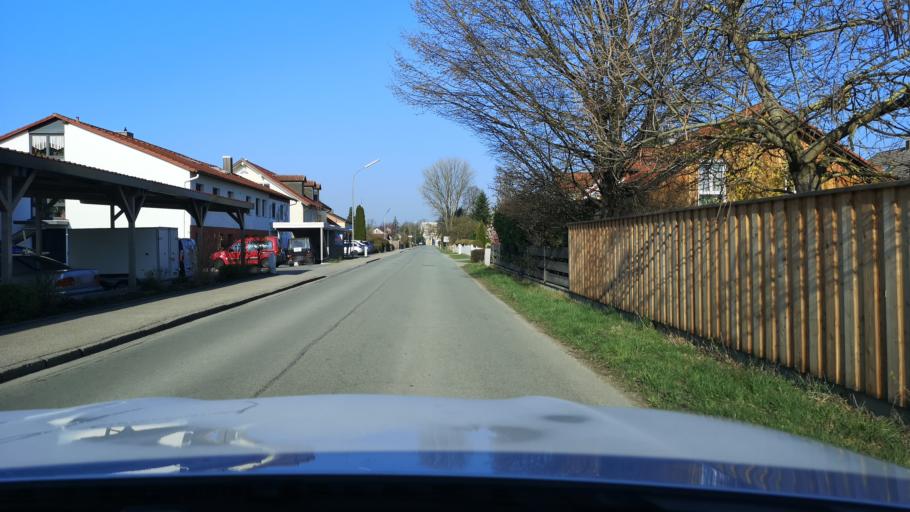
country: DE
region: Bavaria
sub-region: Upper Bavaria
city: Finsing
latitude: 48.2197
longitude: 11.8084
